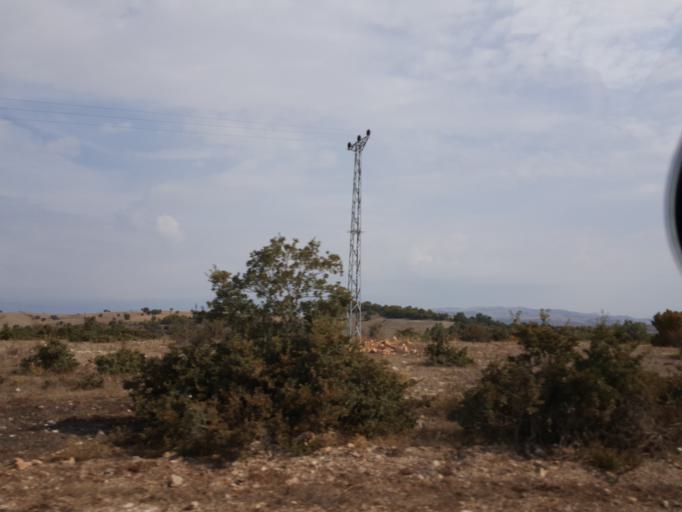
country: TR
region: Tokat
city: Zile
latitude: 40.3761
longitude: 35.8628
